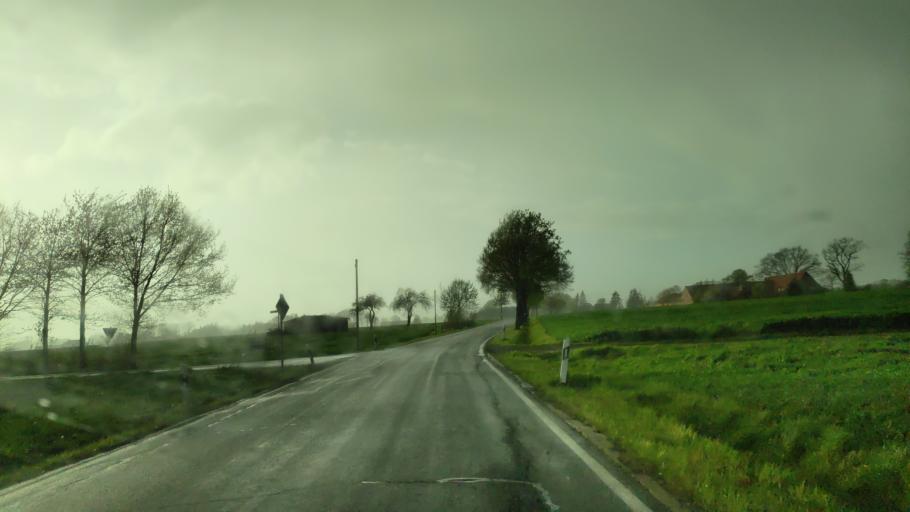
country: DE
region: North Rhine-Westphalia
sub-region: Regierungsbezirk Detmold
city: Hille
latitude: 52.3461
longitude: 8.8245
